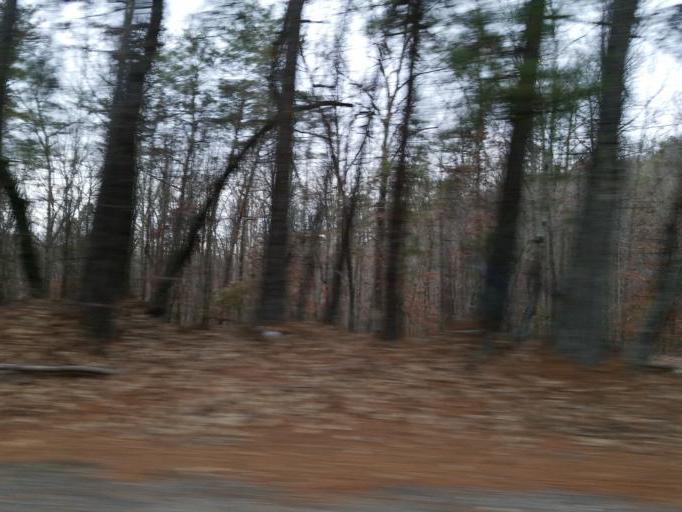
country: US
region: Georgia
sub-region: Dawson County
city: Dawsonville
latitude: 34.4116
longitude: -84.0225
